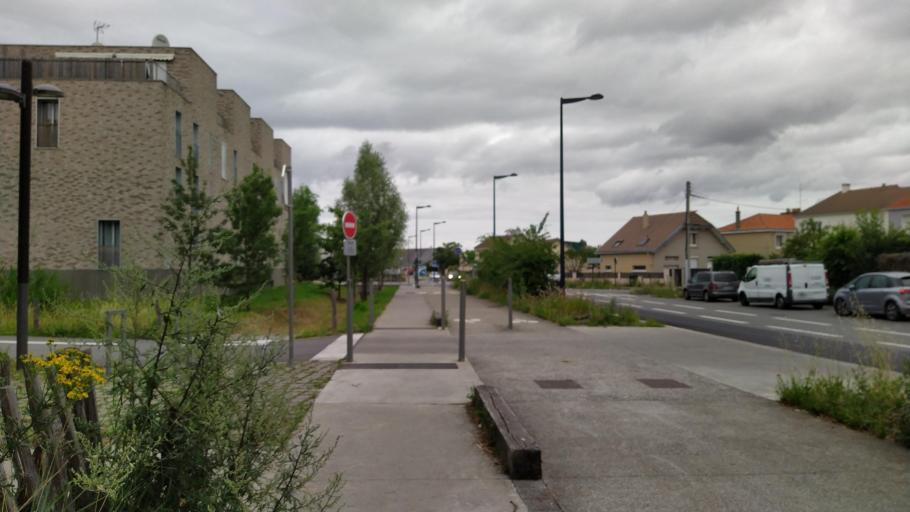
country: FR
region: Pays de la Loire
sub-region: Departement de la Loire-Atlantique
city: Sainte-Luce-sur-Loire
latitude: 47.2377
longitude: -1.5079
